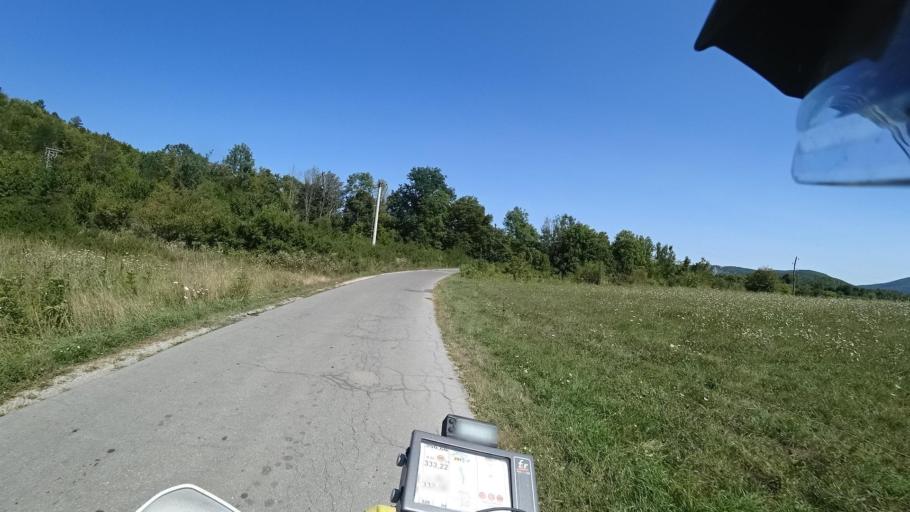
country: HR
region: Licko-Senjska
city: Popovaca
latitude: 44.7234
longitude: 15.2765
